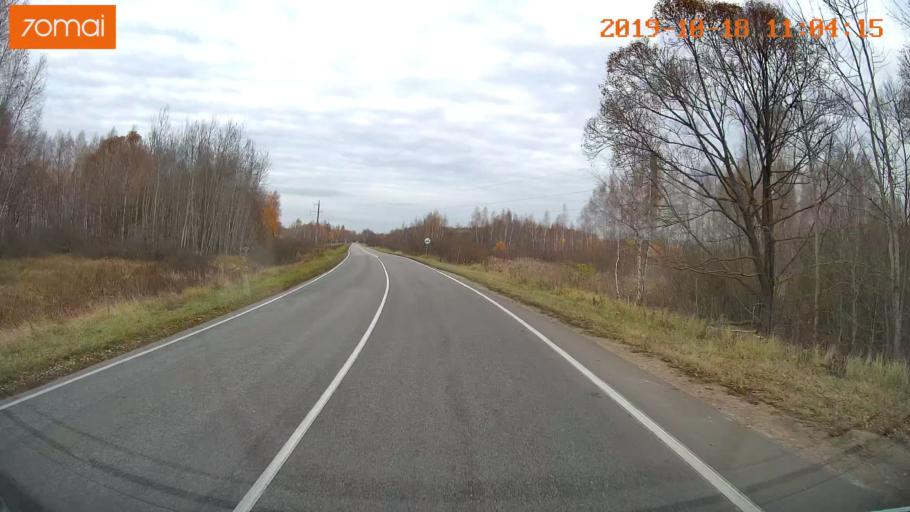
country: RU
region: Tula
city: Yepifan'
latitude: 53.8918
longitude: 38.5504
